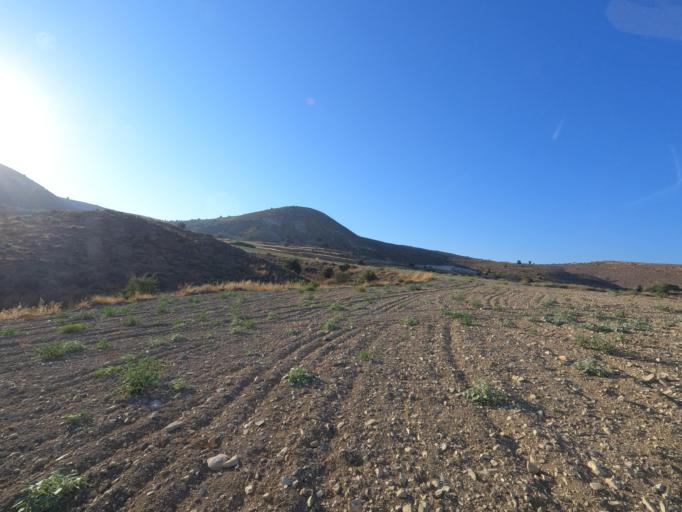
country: CY
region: Larnaka
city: Troulloi
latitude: 35.0262
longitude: 33.6513
